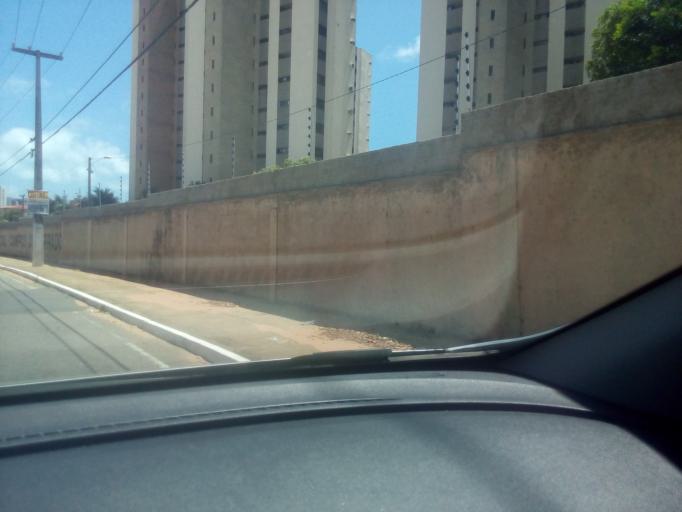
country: BR
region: Rio Grande do Norte
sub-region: Parnamirim
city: Parnamirim
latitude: -5.8950
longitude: -35.1943
